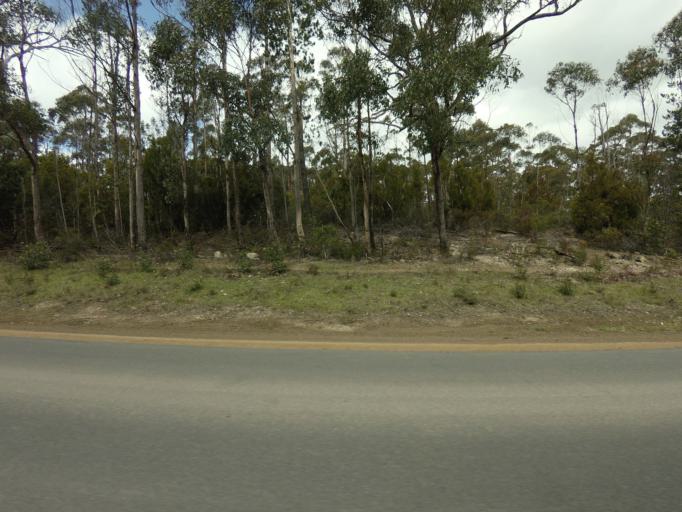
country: AU
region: Tasmania
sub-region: Huon Valley
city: Geeveston
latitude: -43.3238
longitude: 146.9819
